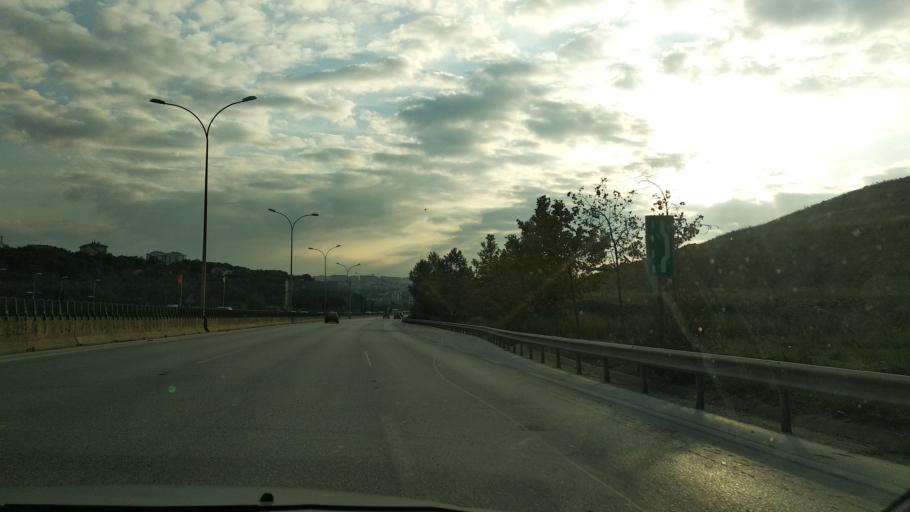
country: TR
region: Istanbul
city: Icmeler
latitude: 40.8868
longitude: 29.3235
